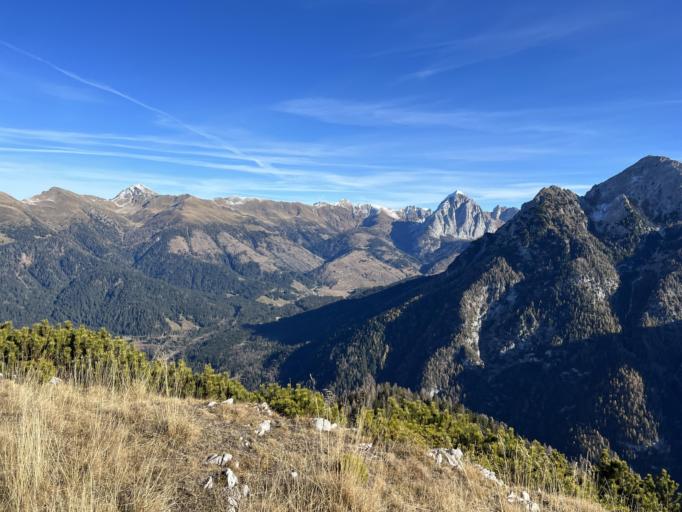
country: IT
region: Veneto
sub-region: Provincia di Belluno
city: San Pietro di Cadore
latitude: 46.5953
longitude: 12.6143
